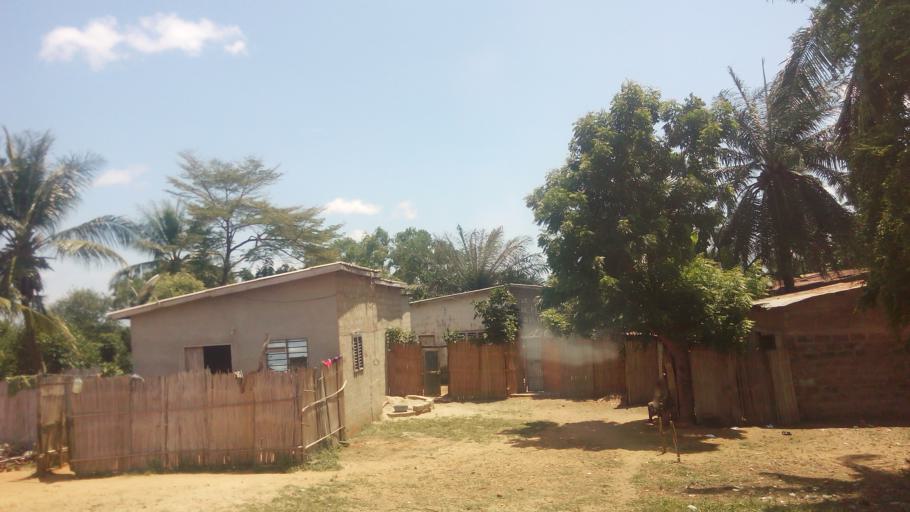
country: BJ
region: Mono
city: Come
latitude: 6.3983
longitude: 1.9251
